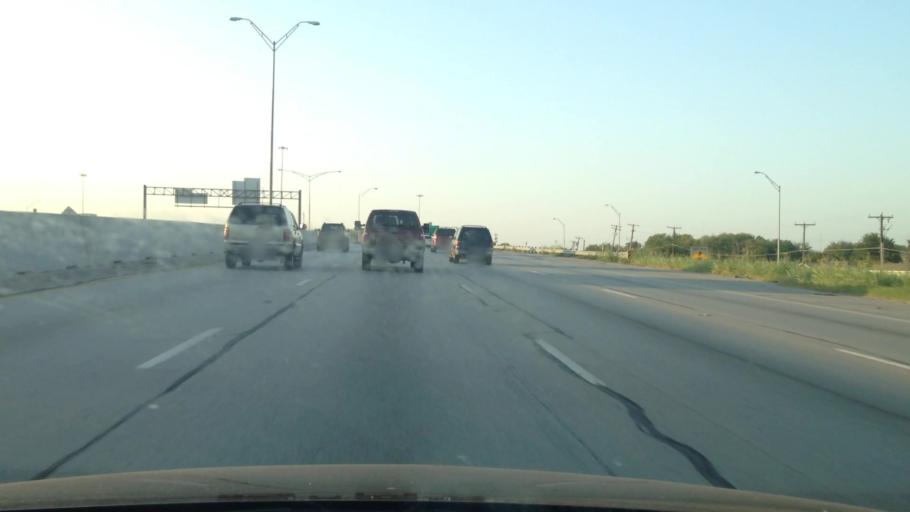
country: US
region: Texas
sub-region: Tarrant County
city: Forest Hill
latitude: 32.6870
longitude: -97.2404
